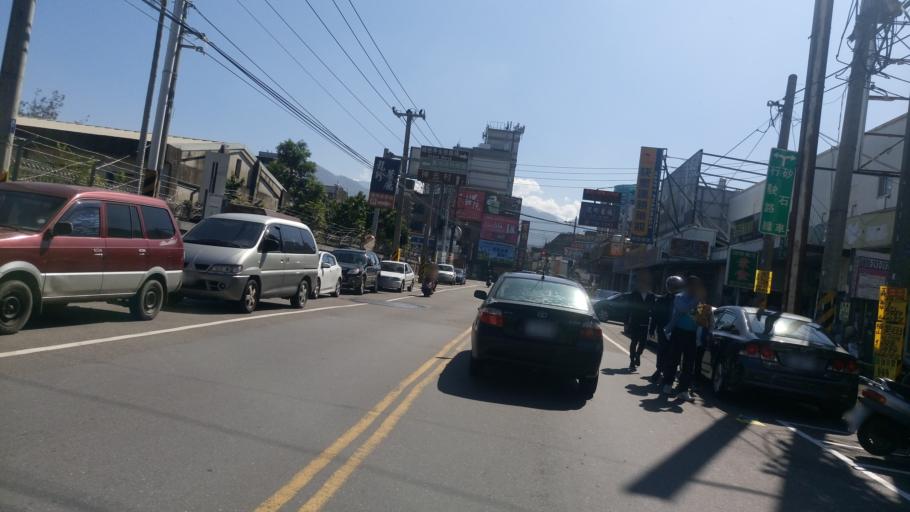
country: TW
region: Taiwan
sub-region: Hsinchu
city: Zhubei
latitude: 24.7233
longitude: 121.0957
